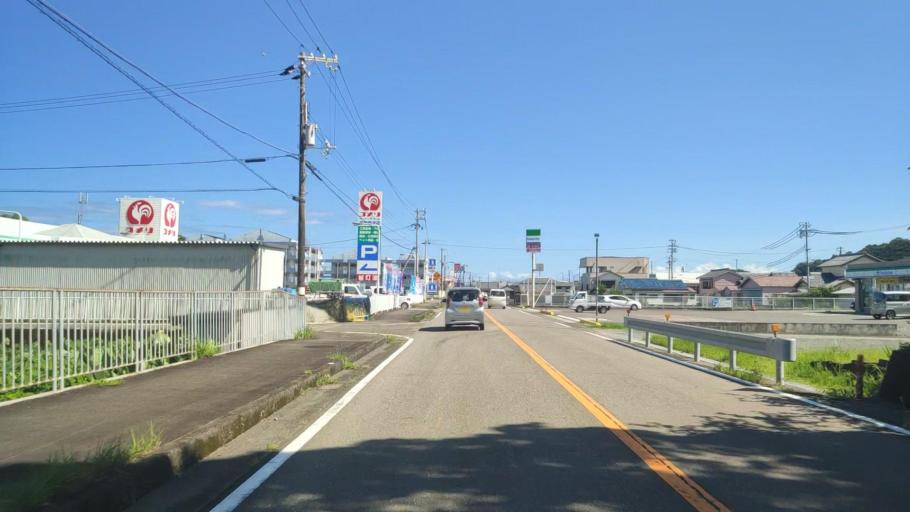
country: JP
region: Wakayama
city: Shingu
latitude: 33.5843
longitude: 135.9192
